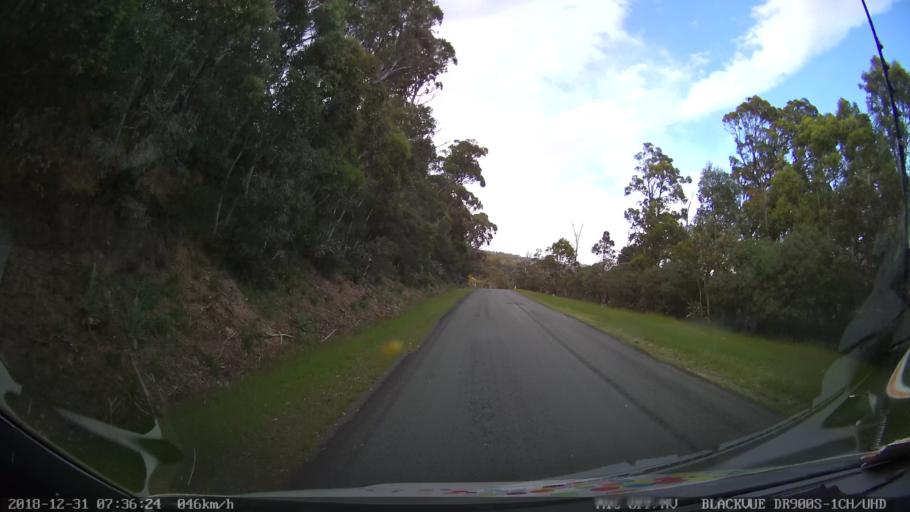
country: AU
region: New South Wales
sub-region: Snowy River
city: Jindabyne
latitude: -36.3407
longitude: 148.4429
